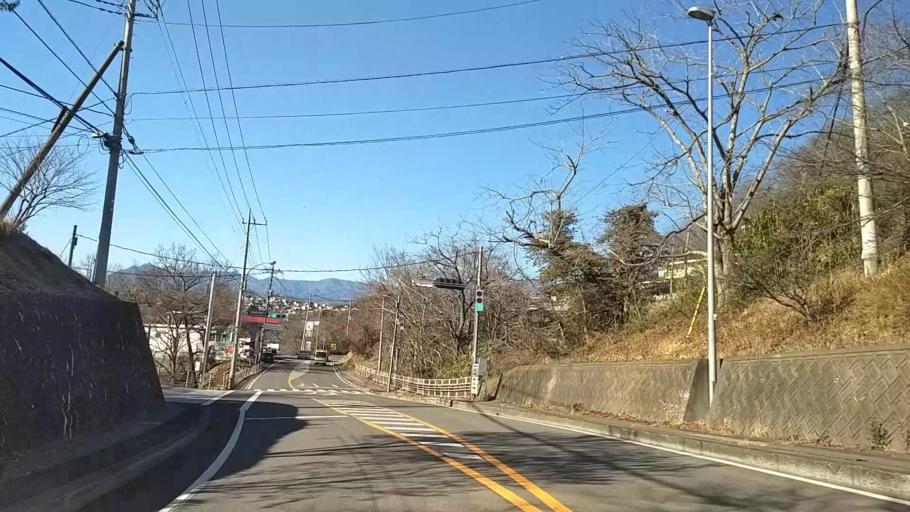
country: JP
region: Yamanashi
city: Otsuki
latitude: 35.6101
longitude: 138.9976
